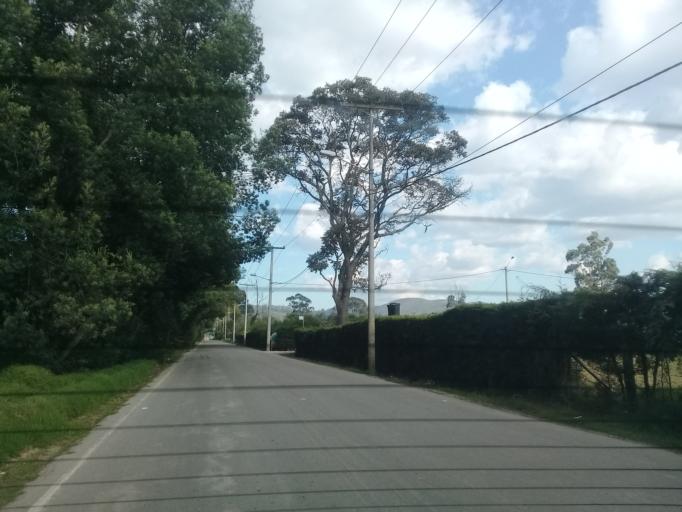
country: CO
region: Cundinamarca
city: El Rosal
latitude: 4.8183
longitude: -74.2361
